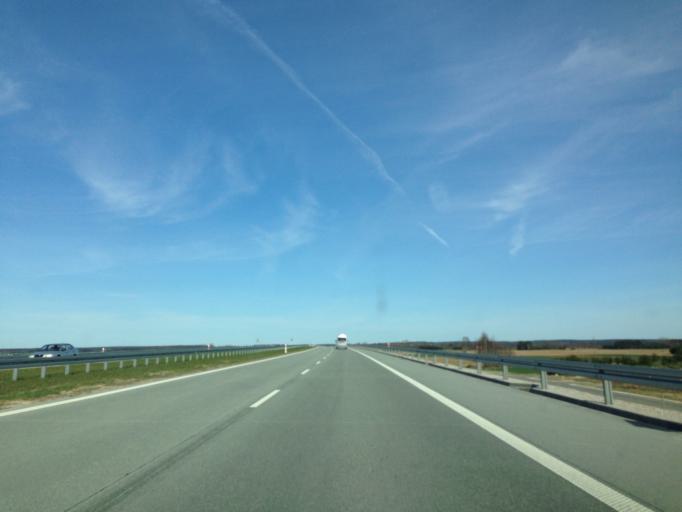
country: PL
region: Lodz Voivodeship
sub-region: Powiat sieradzki
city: Sieradz
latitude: 51.5668
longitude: 18.7754
